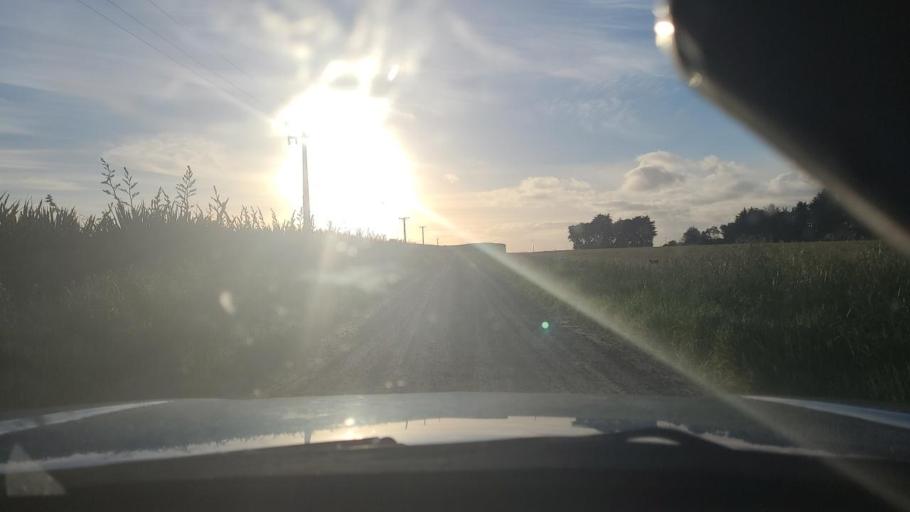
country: NZ
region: Southland
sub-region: Invercargill City
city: Invercargill
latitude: -46.4800
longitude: 168.7106
